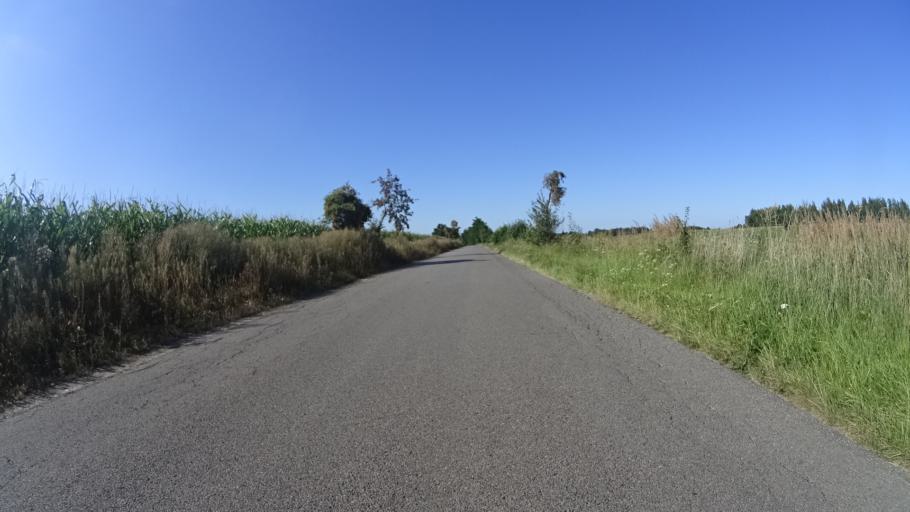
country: PL
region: Masovian Voivodeship
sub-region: Powiat bialobrzeski
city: Wysmierzyce
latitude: 51.6681
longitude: 20.8313
